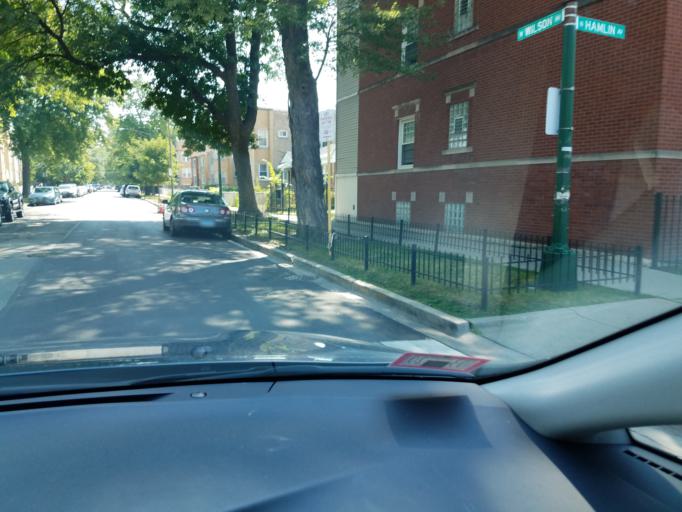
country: US
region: Illinois
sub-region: Cook County
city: Lincolnwood
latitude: 41.9646
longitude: -87.7230
